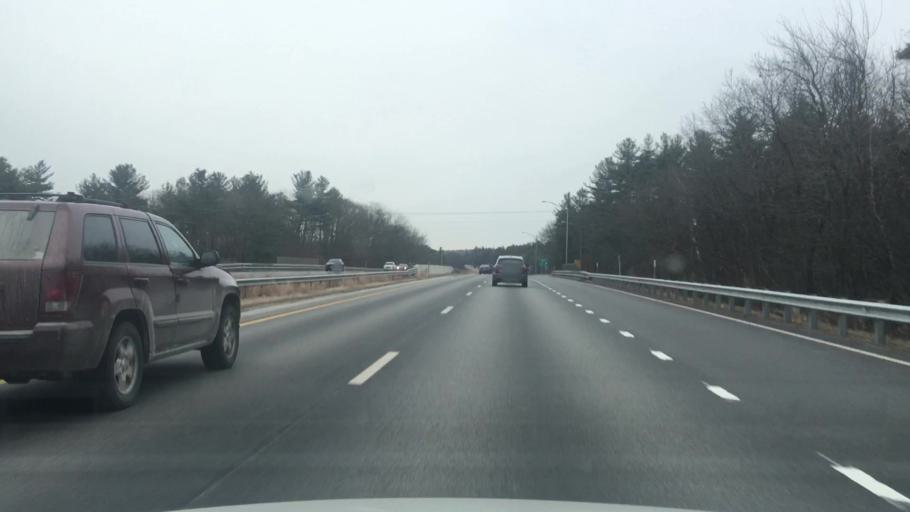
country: US
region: New Hampshire
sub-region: Merrimack County
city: Concord
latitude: 43.1804
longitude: -71.5683
